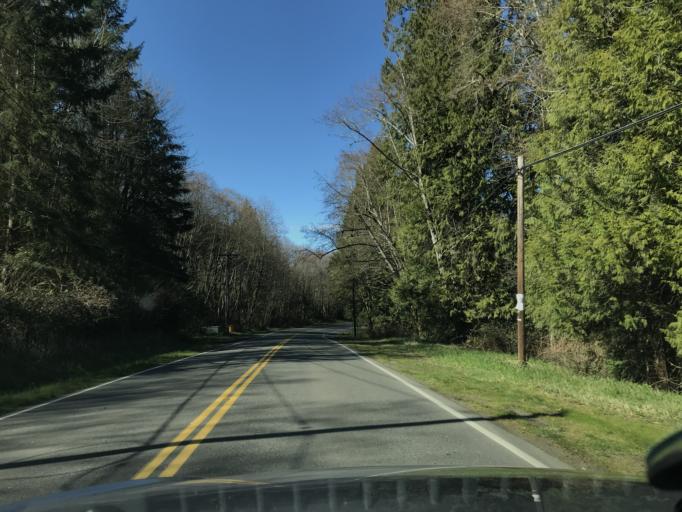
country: US
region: Washington
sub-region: Pierce County
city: Canterwood
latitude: 47.3539
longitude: -122.6106
